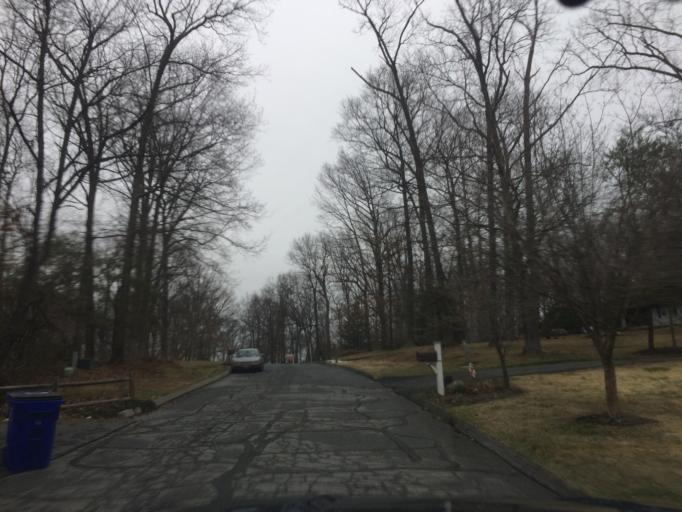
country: US
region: Maryland
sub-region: Howard County
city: Highland
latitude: 39.2078
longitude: -76.9637
